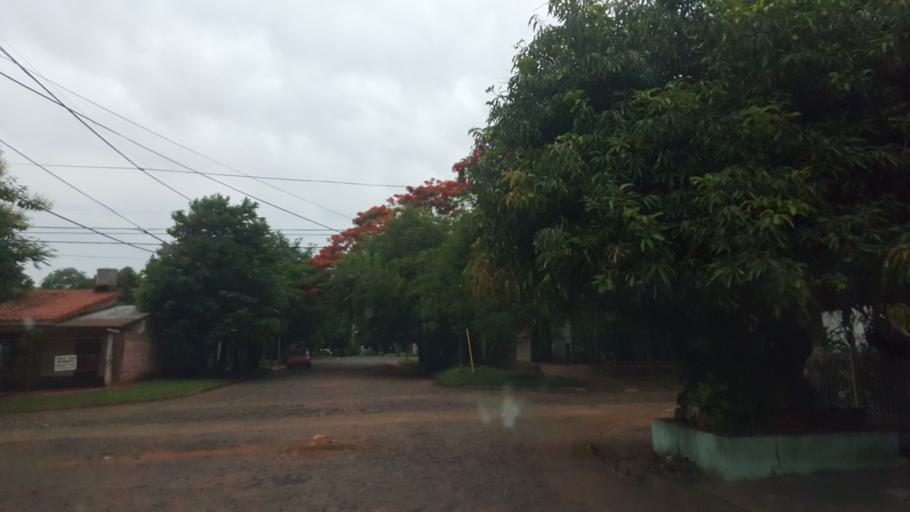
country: AR
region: Misiones
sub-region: Departamento de Capital
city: Posadas
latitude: -27.3774
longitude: -55.9236
